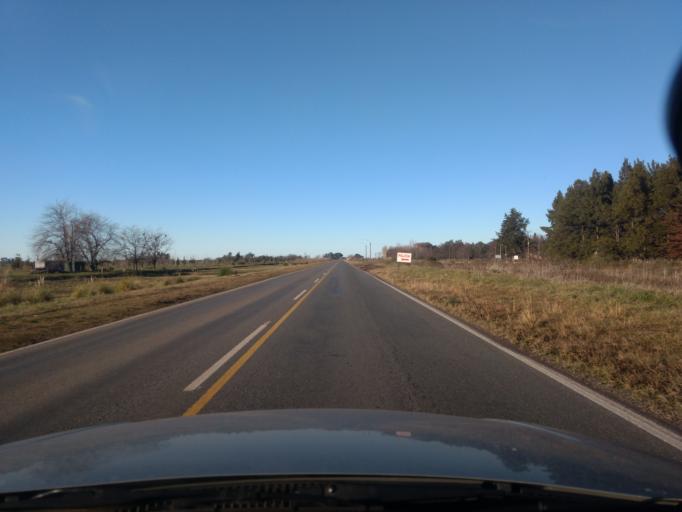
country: AR
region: Buenos Aires
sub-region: Partido de Lujan
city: Lujan
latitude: -34.6576
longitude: -59.1017
